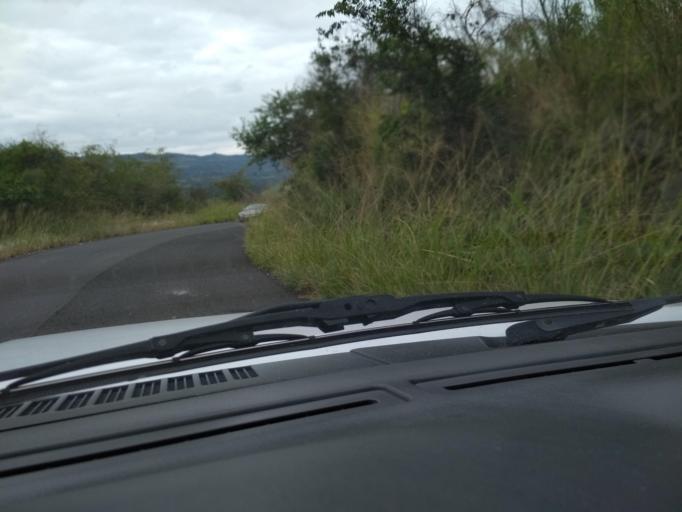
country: MX
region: Veracruz
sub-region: Actopan
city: Trapiche del Rosario
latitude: 19.5827
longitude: -96.7928
